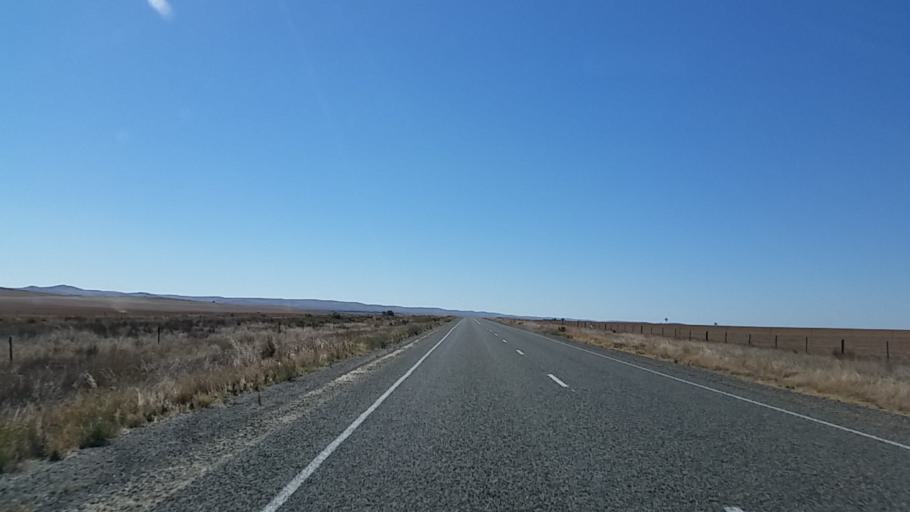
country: AU
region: South Australia
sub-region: Northern Areas
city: Jamestown
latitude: -33.2808
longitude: 138.8688
